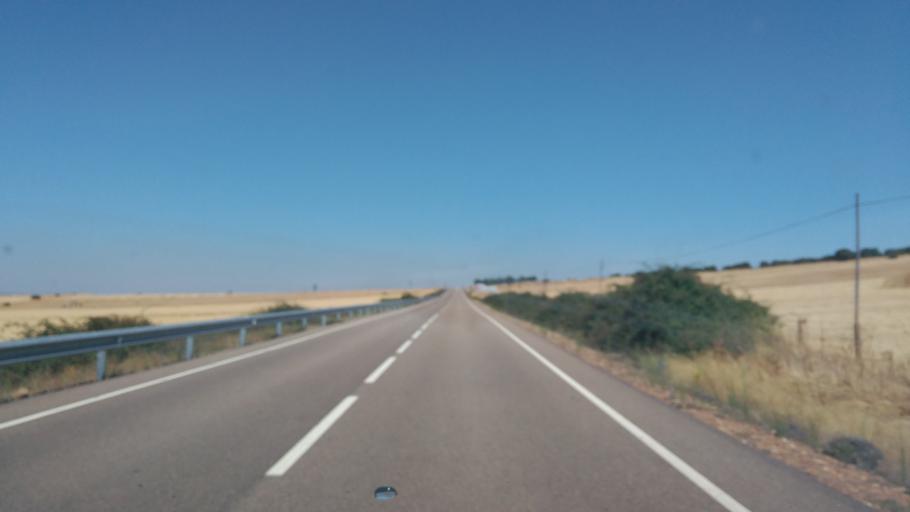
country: ES
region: Castille and Leon
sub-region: Provincia de Salamanca
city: Tamames
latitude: 40.6505
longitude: -6.1159
